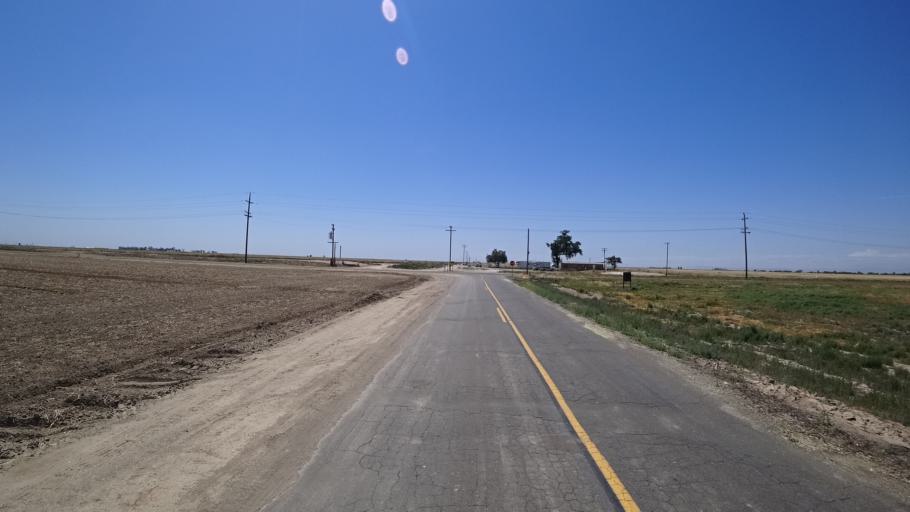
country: US
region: California
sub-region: Kings County
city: Armona
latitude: 36.2262
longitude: -119.7266
